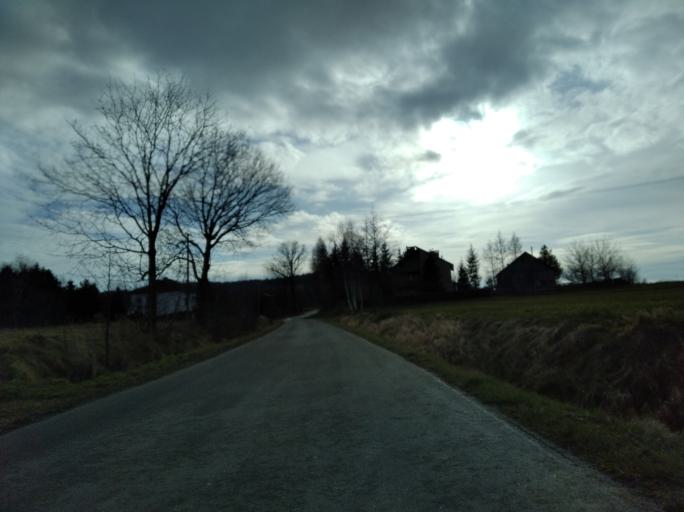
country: PL
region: Subcarpathian Voivodeship
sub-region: Powiat strzyzowski
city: Strzyzow
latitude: 49.8450
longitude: 21.7764
